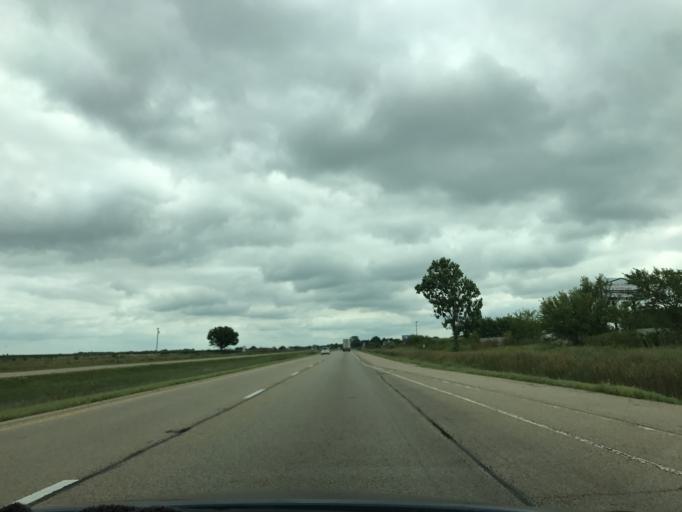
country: US
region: Illinois
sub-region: Bureau County
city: Ladd
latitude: 41.3666
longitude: -89.2133
